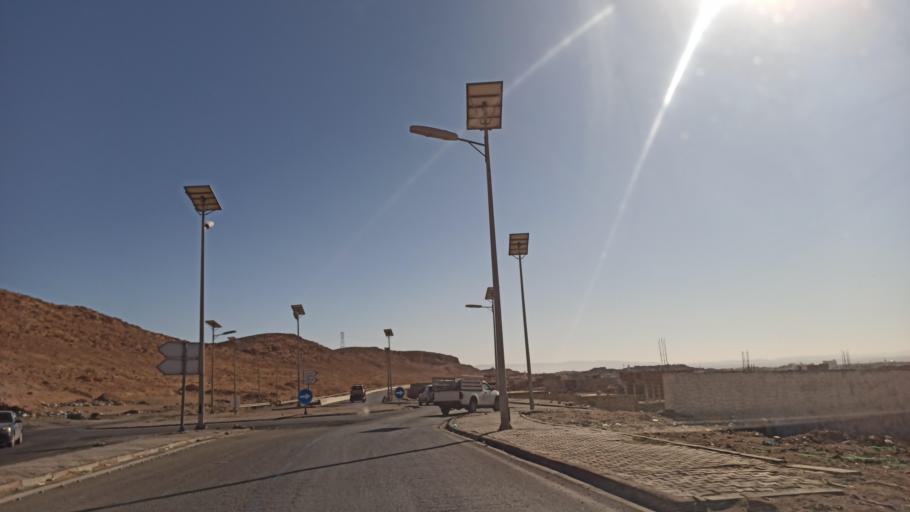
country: TN
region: Gafsa
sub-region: Gafsa Municipality
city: Gafsa
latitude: 34.4451
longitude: 8.7879
